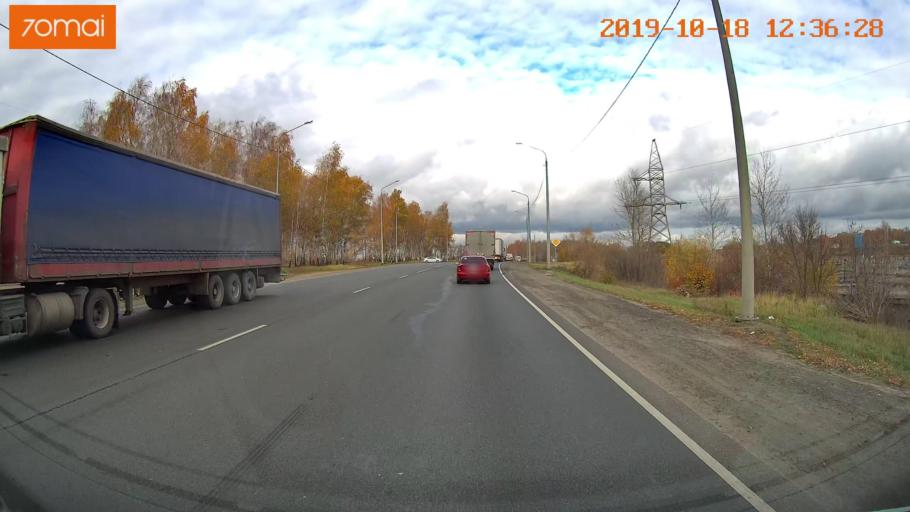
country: RU
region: Rjazan
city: Ryazan'
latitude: 54.6354
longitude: 39.6338
